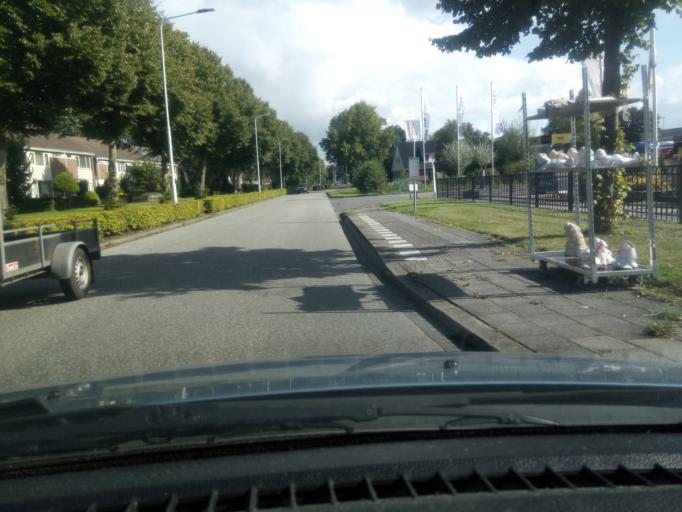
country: NL
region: Friesland
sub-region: Gemeente Achtkarspelen
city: Surhuisterveen
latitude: 53.1819
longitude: 6.1791
